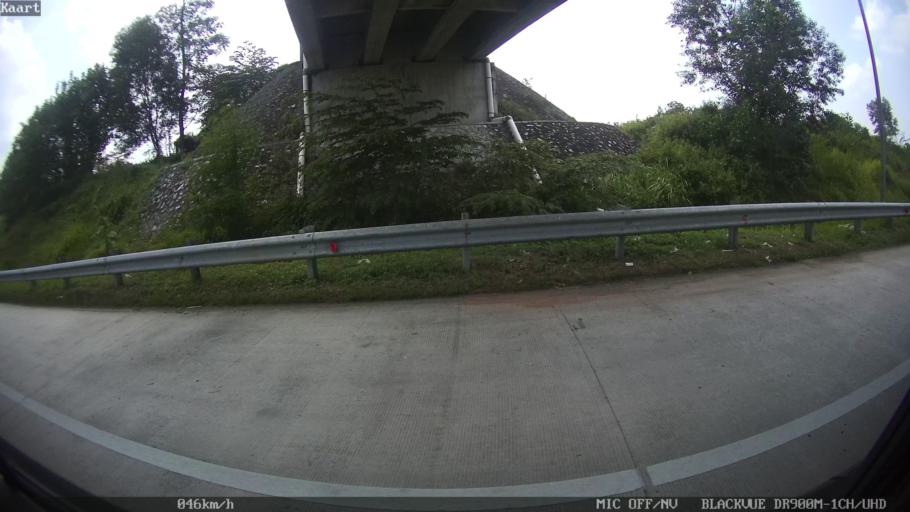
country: ID
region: Lampung
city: Natar
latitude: -5.2765
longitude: 105.2164
